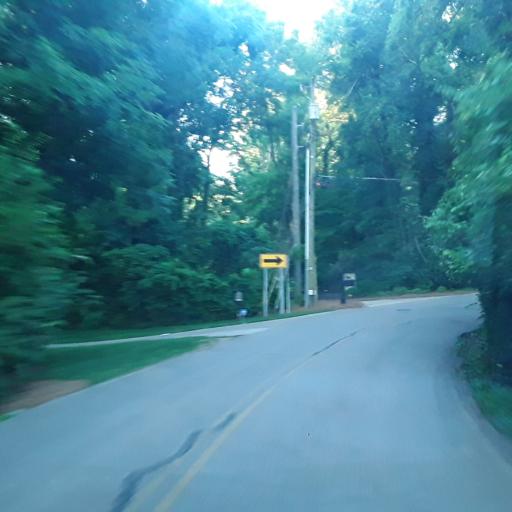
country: US
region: Tennessee
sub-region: Davidson County
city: Oak Hill
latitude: 36.0756
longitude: -86.7820
